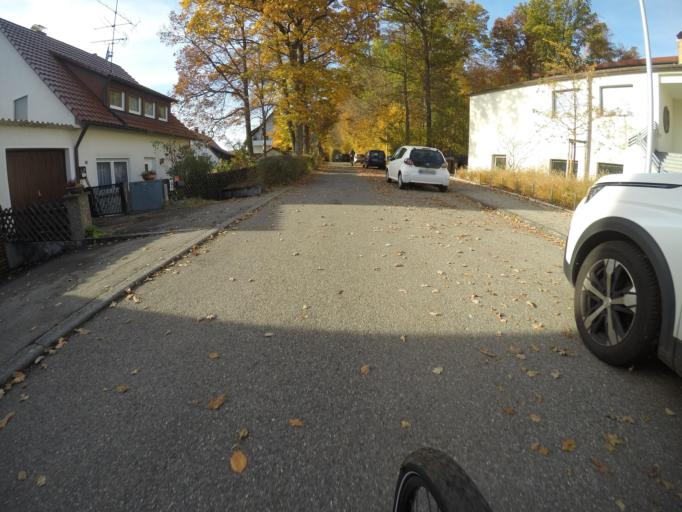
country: DE
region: Baden-Wuerttemberg
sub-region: Regierungsbezirk Stuttgart
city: Leinfelden-Echterdingen
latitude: 48.6945
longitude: 9.1357
